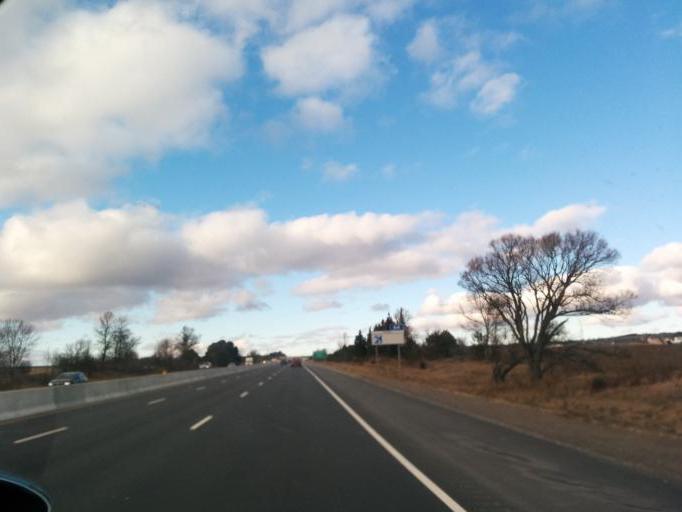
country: CA
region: Ontario
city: Bradford West Gwillimbury
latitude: 44.0882
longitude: -79.6279
